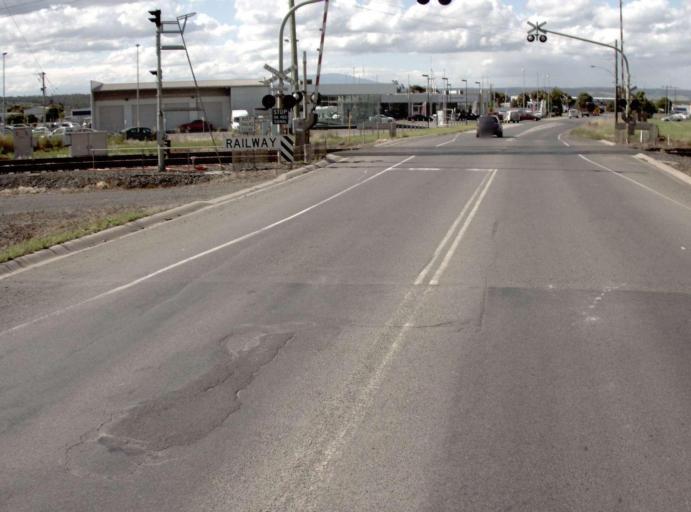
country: AU
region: Victoria
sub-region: Latrobe
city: Morwell
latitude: -38.2363
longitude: 146.4383
